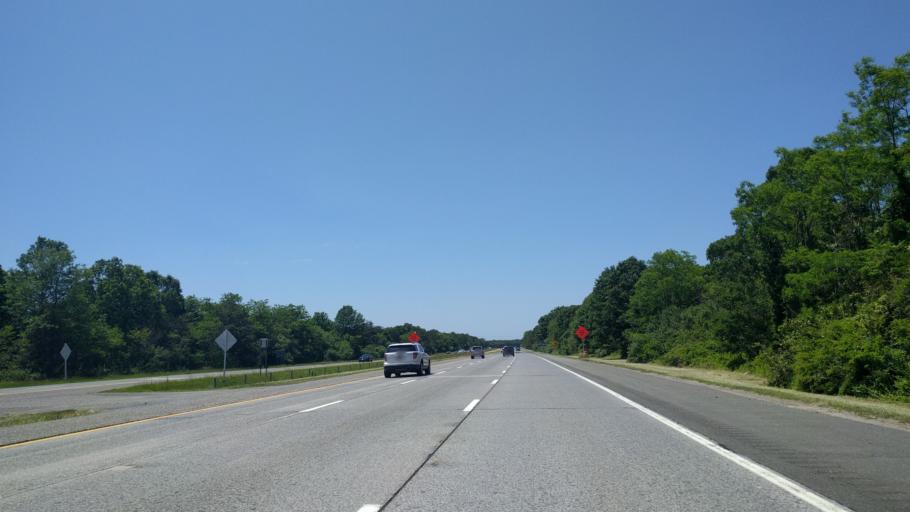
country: US
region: New York
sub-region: Suffolk County
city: Manorville
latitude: 40.8602
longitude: -72.8312
